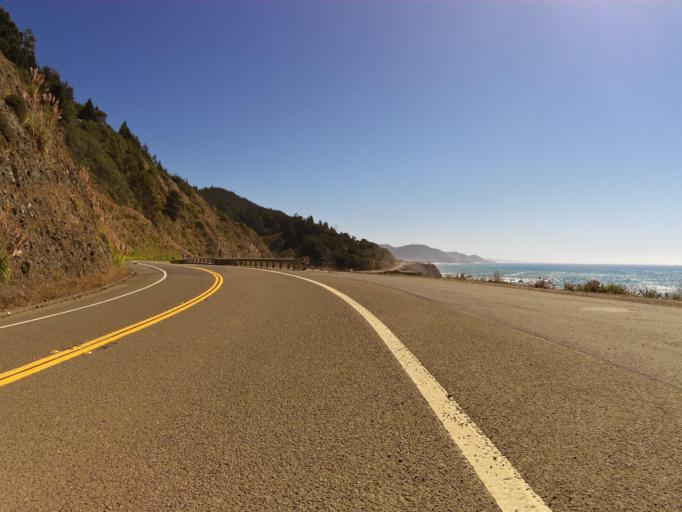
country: US
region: California
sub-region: Mendocino County
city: Fort Bragg
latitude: 39.7072
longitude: -123.8059
